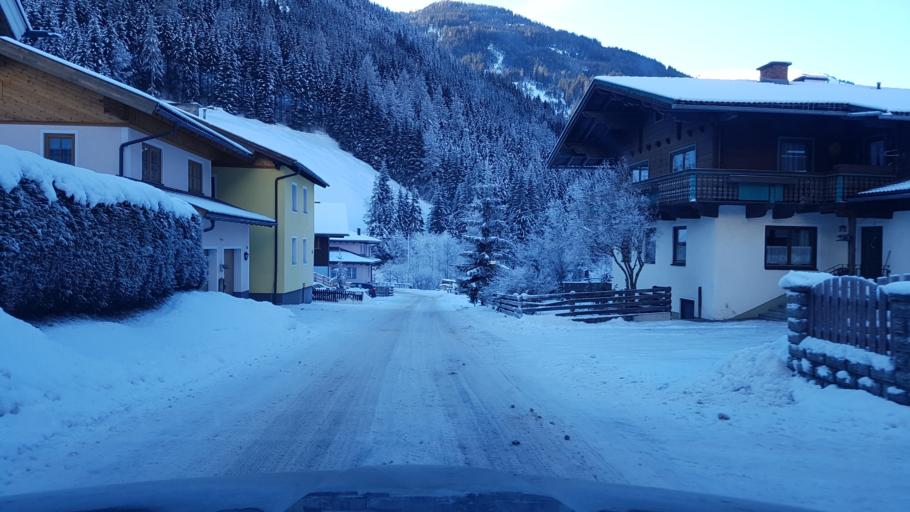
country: AT
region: Salzburg
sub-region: Politischer Bezirk Sankt Johann im Pongau
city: Huttschlag
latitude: 47.1680
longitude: 13.2605
